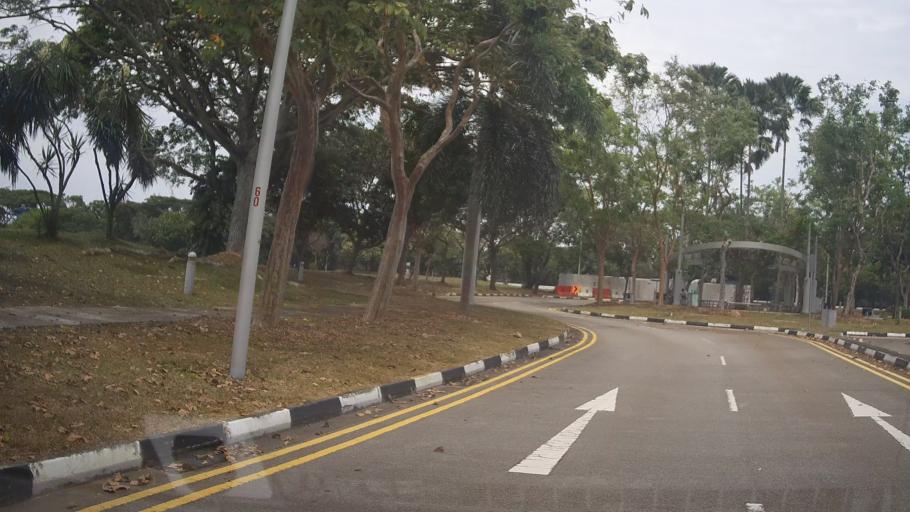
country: SG
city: Singapore
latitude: 1.3412
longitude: 103.9684
